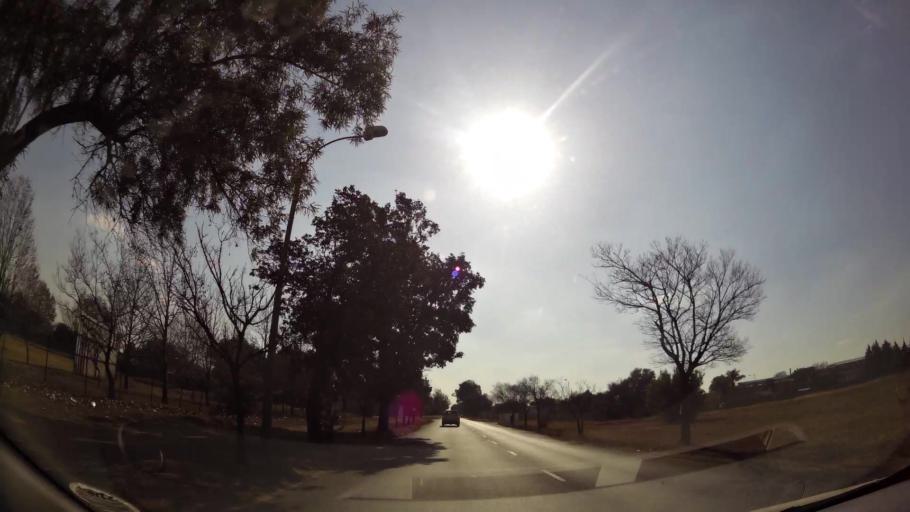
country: ZA
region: Gauteng
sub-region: West Rand District Municipality
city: Randfontein
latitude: -26.1607
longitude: 27.7044
